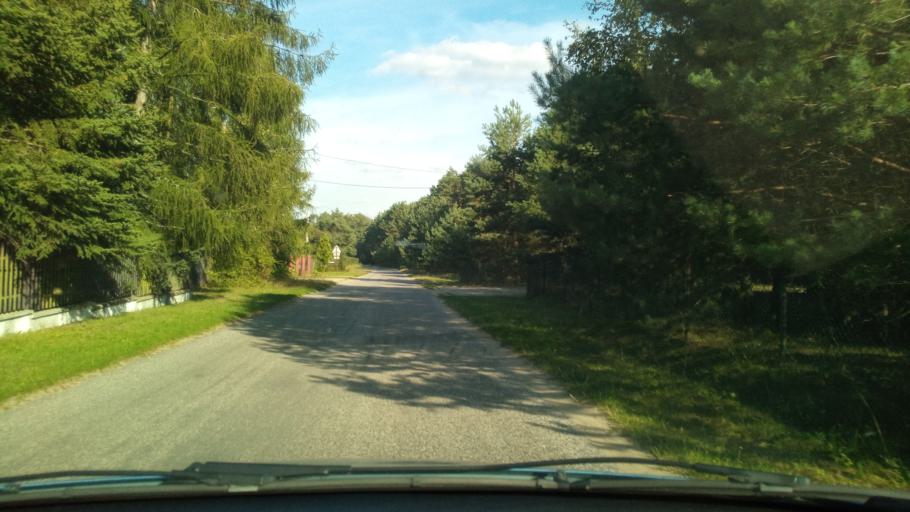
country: PL
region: Lodz Voivodeship
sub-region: Powiat piotrkowski
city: Sulejow
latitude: 51.4094
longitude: 19.8788
